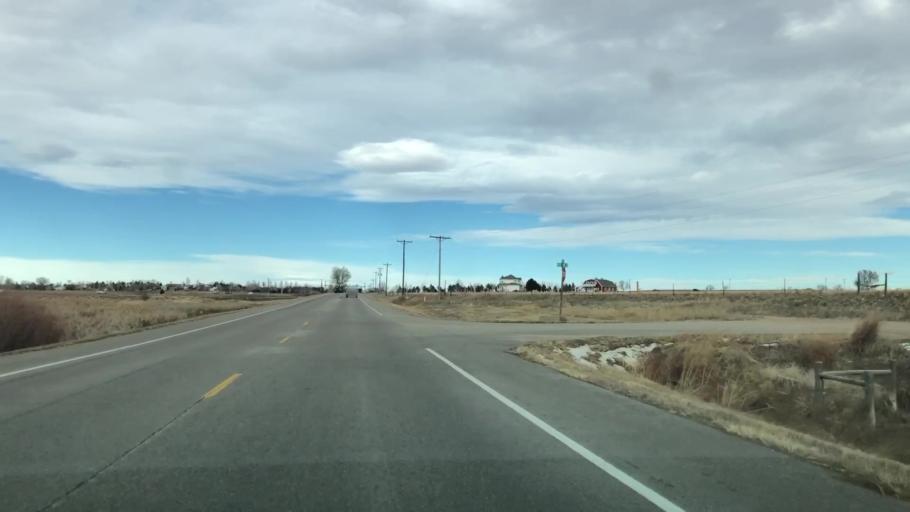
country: US
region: Colorado
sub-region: Weld County
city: Windsor
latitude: 40.5182
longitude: -104.9259
